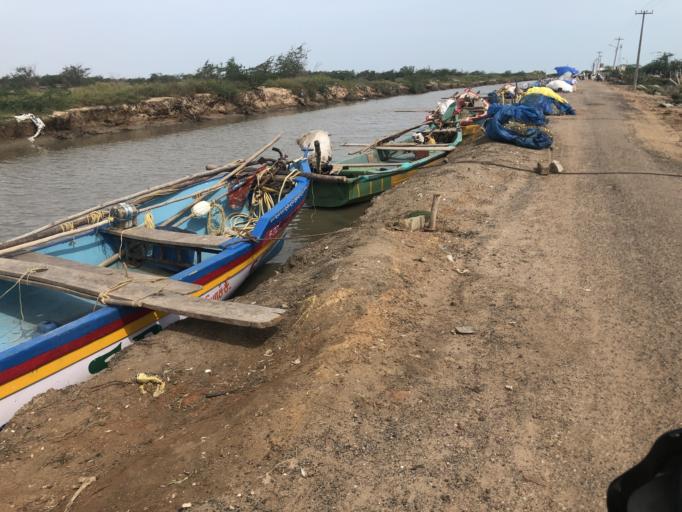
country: IN
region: Tamil Nadu
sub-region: Thanjavur
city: Adirampattinam
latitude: 10.3198
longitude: 79.3803
